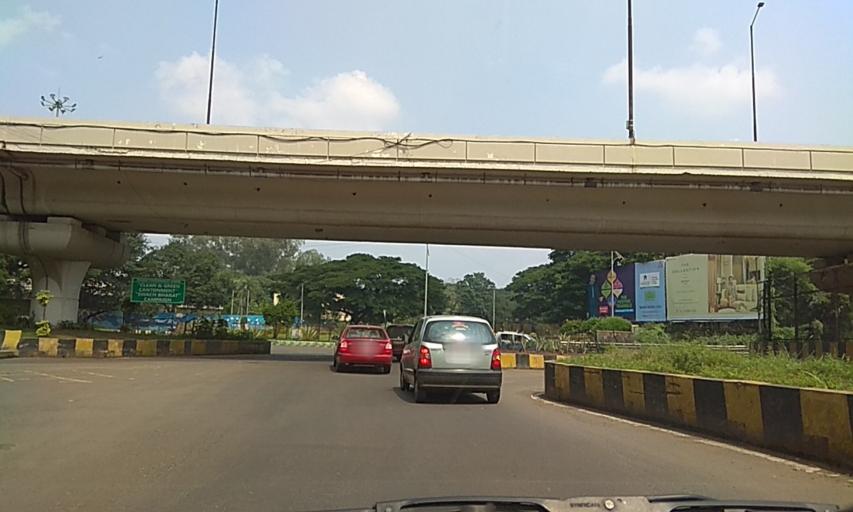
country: IN
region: Maharashtra
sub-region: Pune Division
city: Khadki
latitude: 18.5554
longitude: 73.8613
